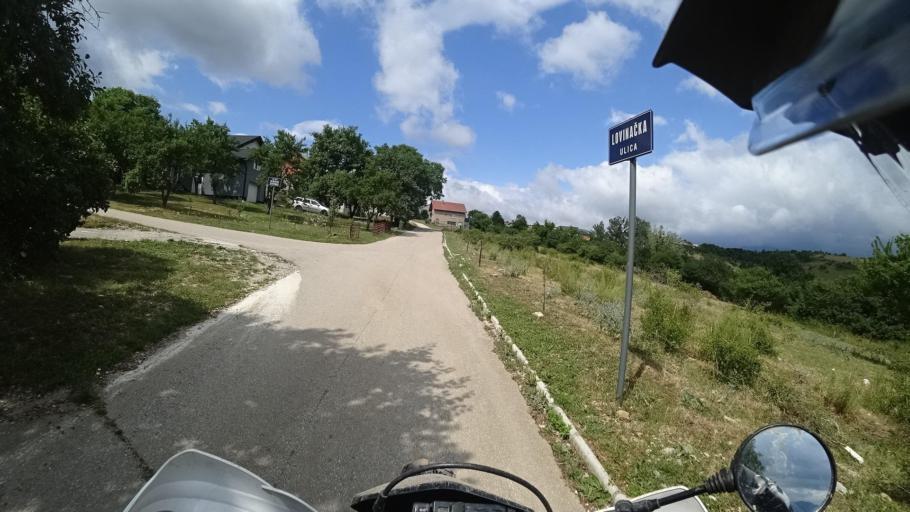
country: HR
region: Zadarska
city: Gracac
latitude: 44.5279
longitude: 15.7659
